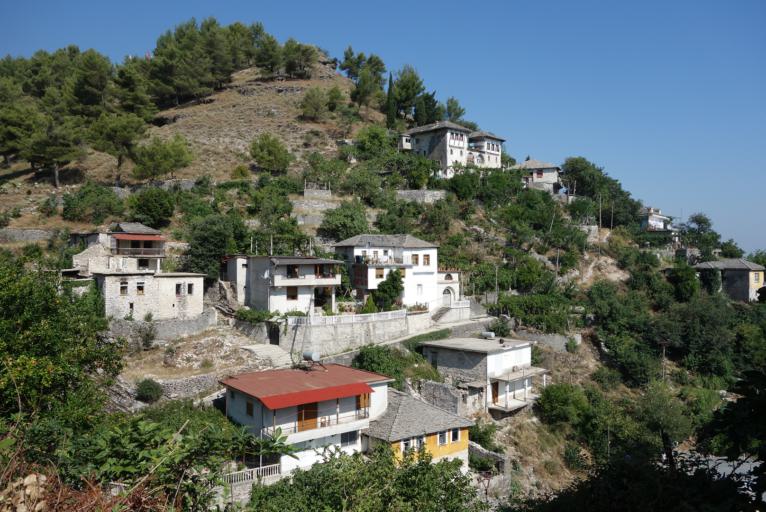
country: AL
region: Gjirokaster
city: Gjirokaster
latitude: 40.0717
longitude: 20.1362
